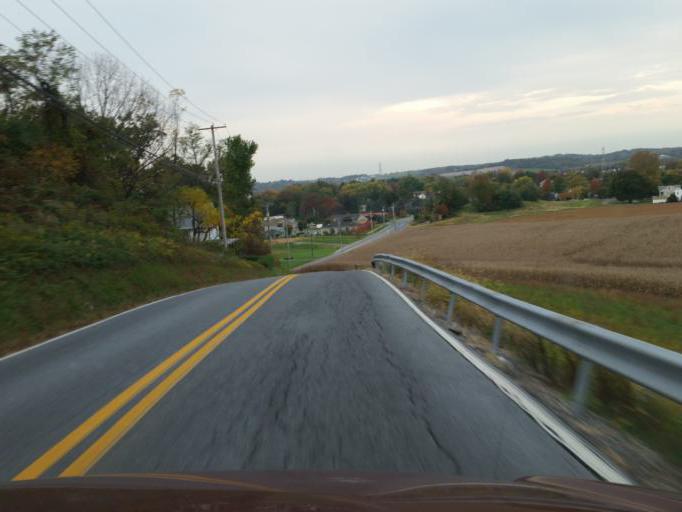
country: US
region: Pennsylvania
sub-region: Dauphin County
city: Hummelstown
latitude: 40.2375
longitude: -76.7057
